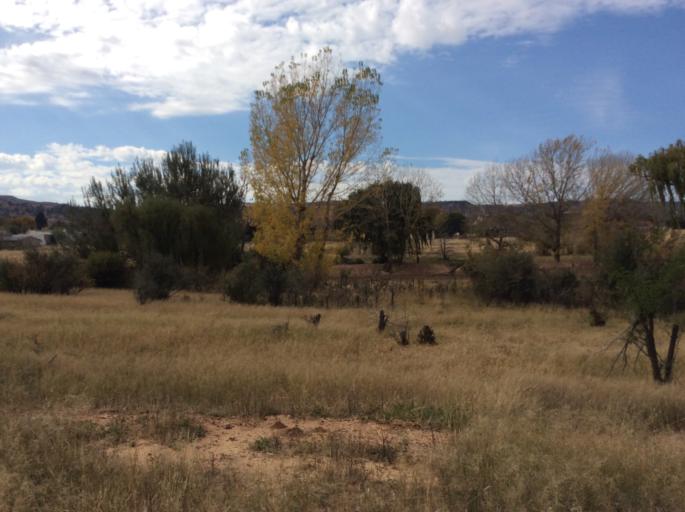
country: LS
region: Mafeteng
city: Mafeteng
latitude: -29.7288
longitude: 27.0323
